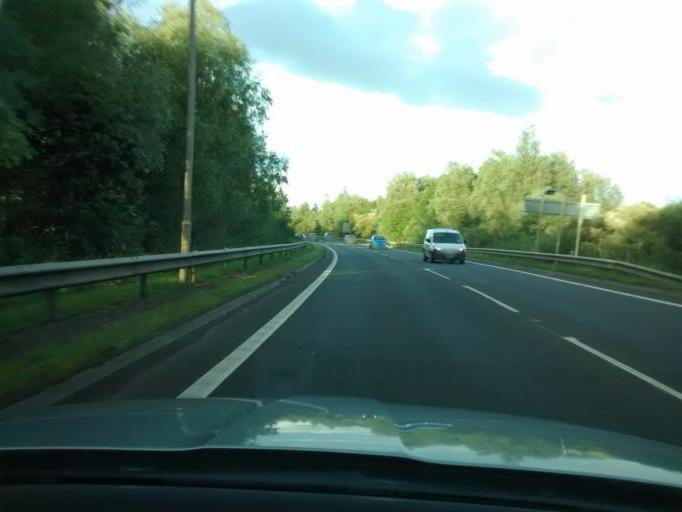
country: GB
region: Scotland
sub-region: Renfrewshire
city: Howwood
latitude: 55.8066
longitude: -4.5704
